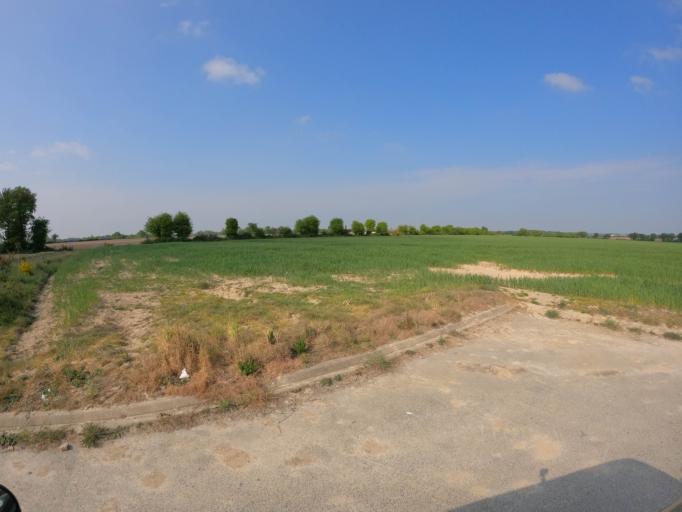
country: FR
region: Pays de la Loire
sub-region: Departement de la Vendee
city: La Bruffiere
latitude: 46.9981
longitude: -1.1711
